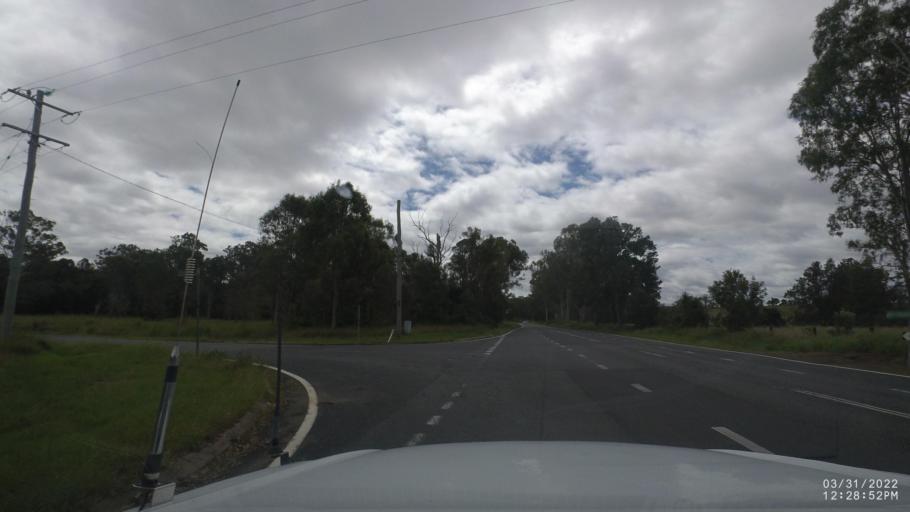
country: AU
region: Queensland
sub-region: Logan
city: Cedar Vale
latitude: -27.9291
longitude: 153.0798
